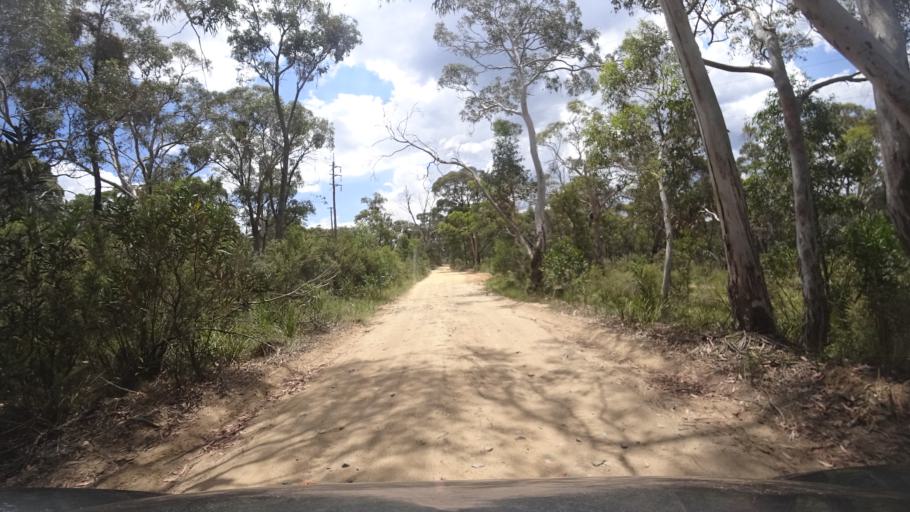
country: AU
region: New South Wales
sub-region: Lithgow
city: Lithgow
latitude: -33.4781
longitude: 150.2459
